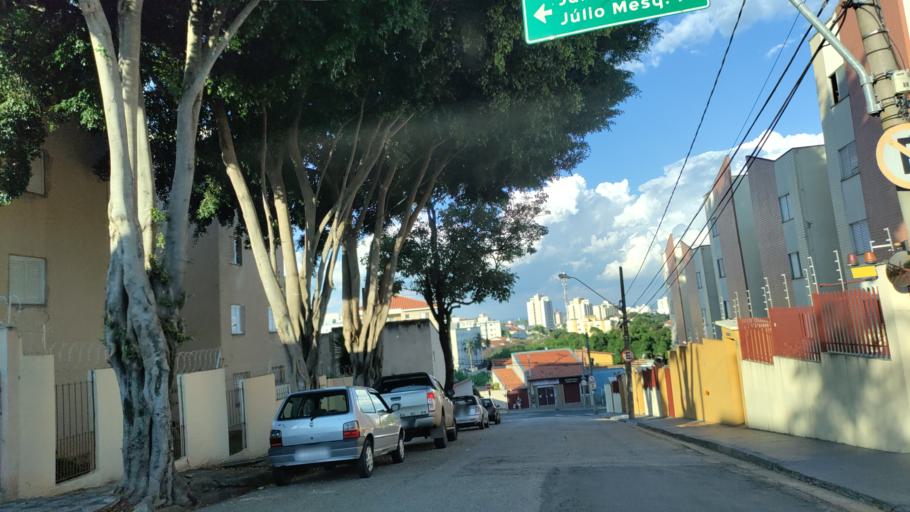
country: BR
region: Sao Paulo
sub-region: Sorocaba
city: Sorocaba
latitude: -23.5092
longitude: -47.4839
